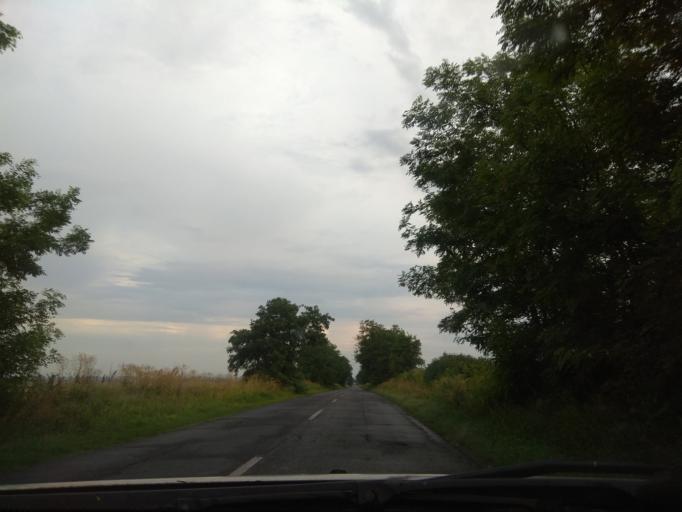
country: HU
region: Borsod-Abauj-Zemplen
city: Gesztely
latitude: 48.1331
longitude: 20.9733
